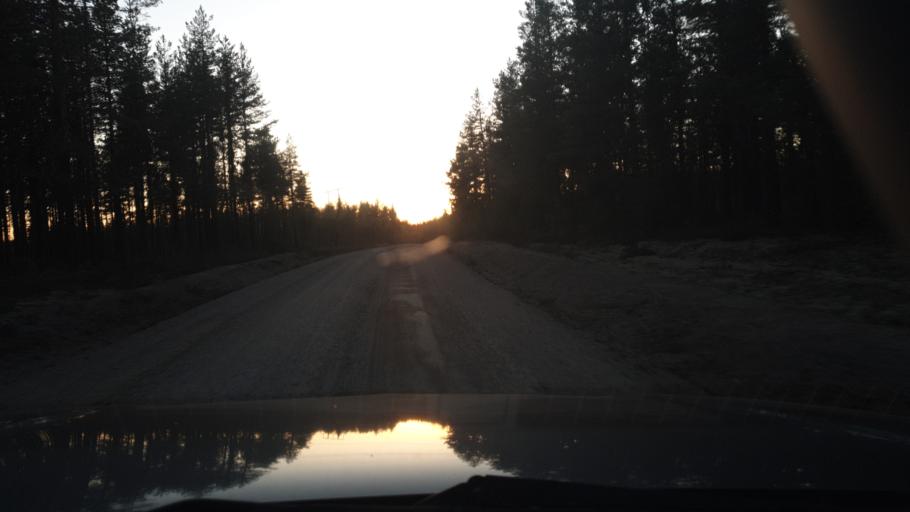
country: SE
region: Vaesternorrland
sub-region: Ange Kommun
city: Ange
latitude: 62.2036
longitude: 15.5542
